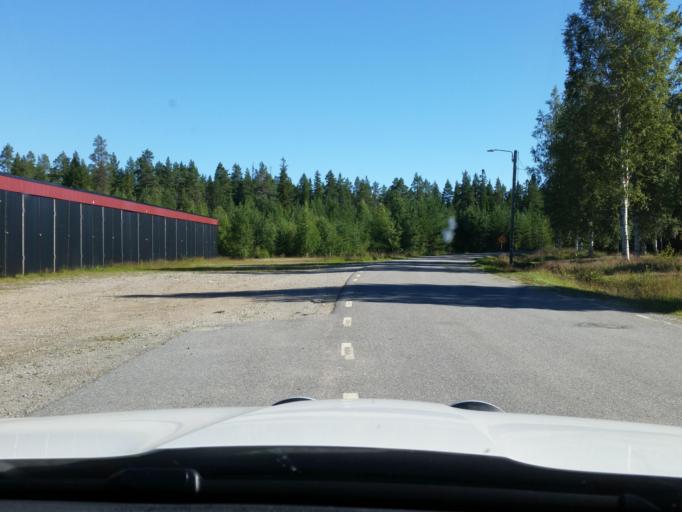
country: SE
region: Norrbotten
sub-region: Pitea Kommun
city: Roknas
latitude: 65.2458
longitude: 21.2526
